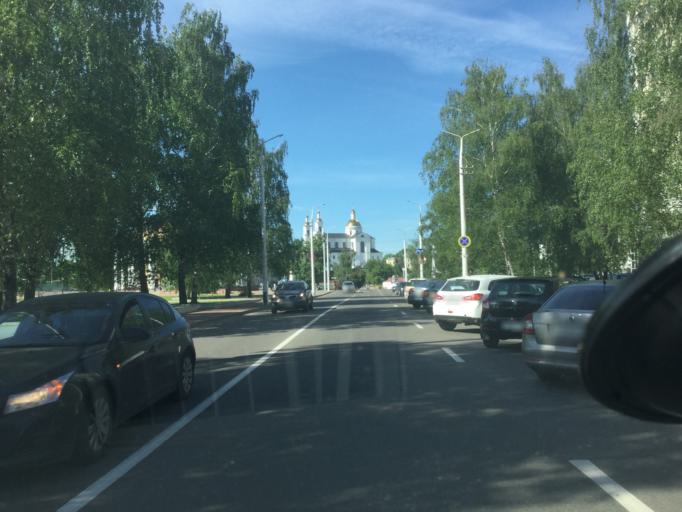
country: BY
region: Vitebsk
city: Vitebsk
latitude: 55.1916
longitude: 30.2018
